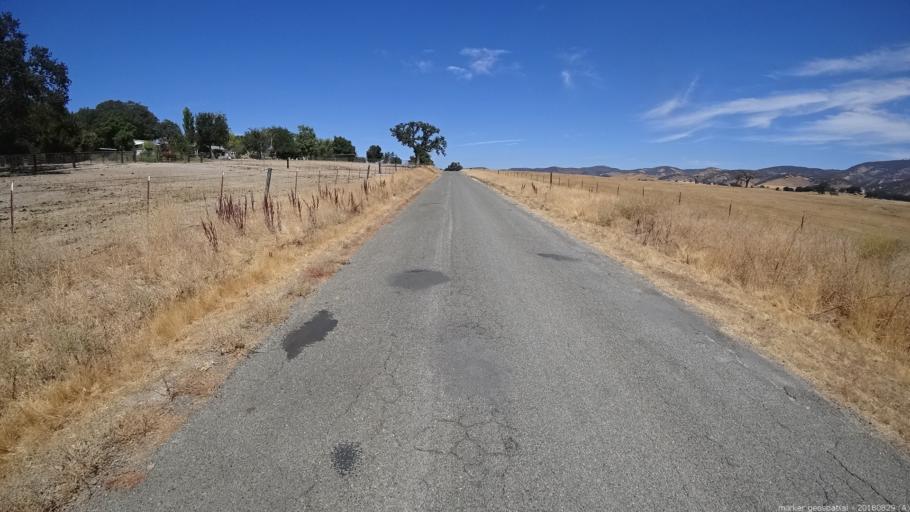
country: US
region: California
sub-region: San Luis Obispo County
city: Lake Nacimiento
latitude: 35.9235
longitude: -121.0643
